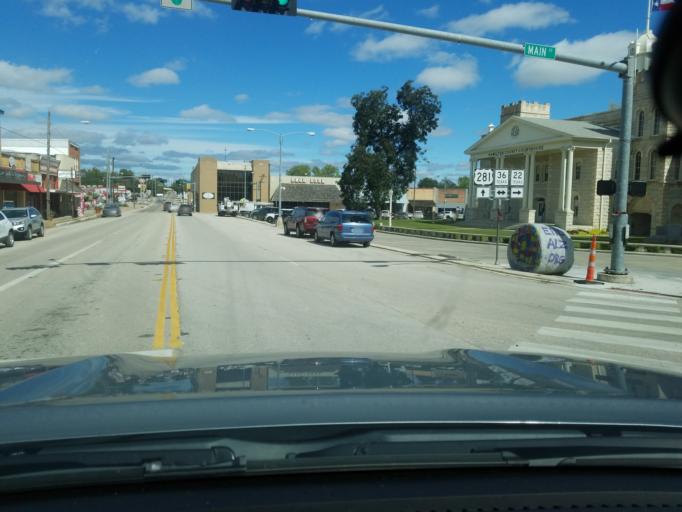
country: US
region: Texas
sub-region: Hamilton County
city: Hamilton
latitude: 31.7038
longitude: -98.1240
